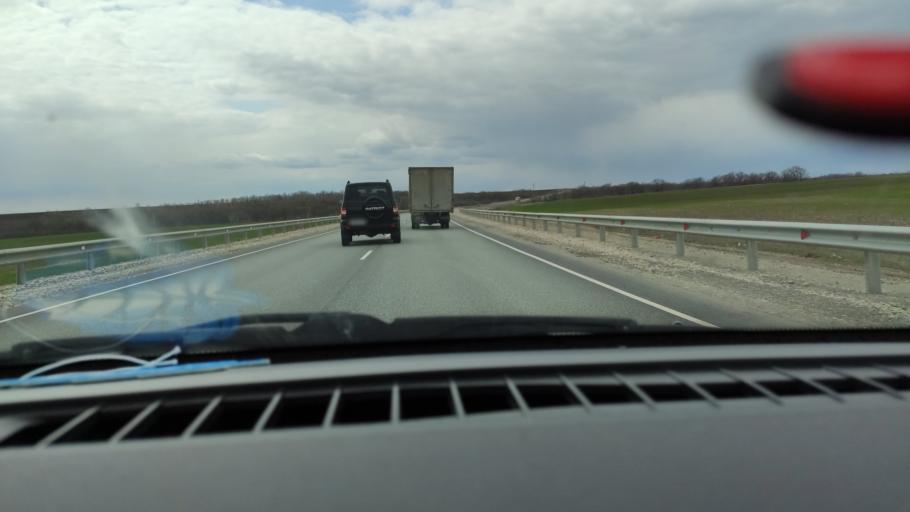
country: RU
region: Saratov
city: Yelshanka
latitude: 51.8311
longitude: 46.4522
